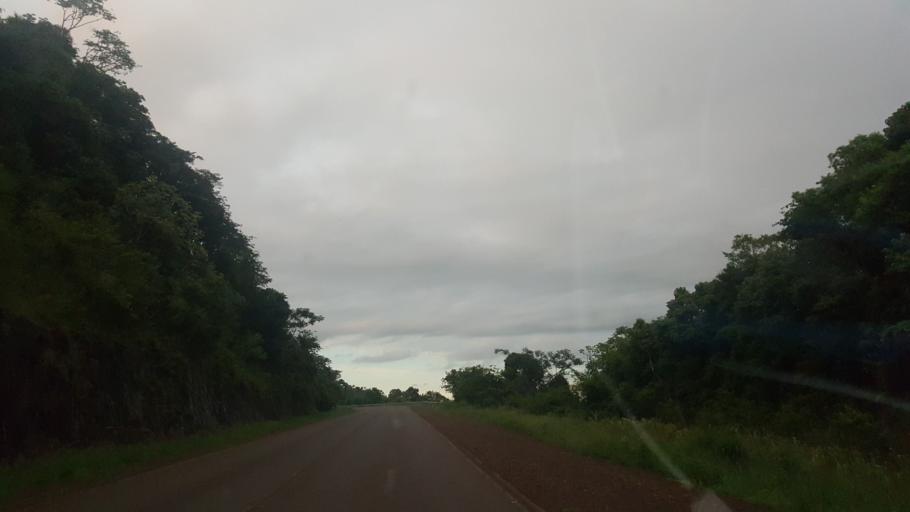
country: AR
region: Misiones
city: Dos de Mayo
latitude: -26.9074
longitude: -54.7389
